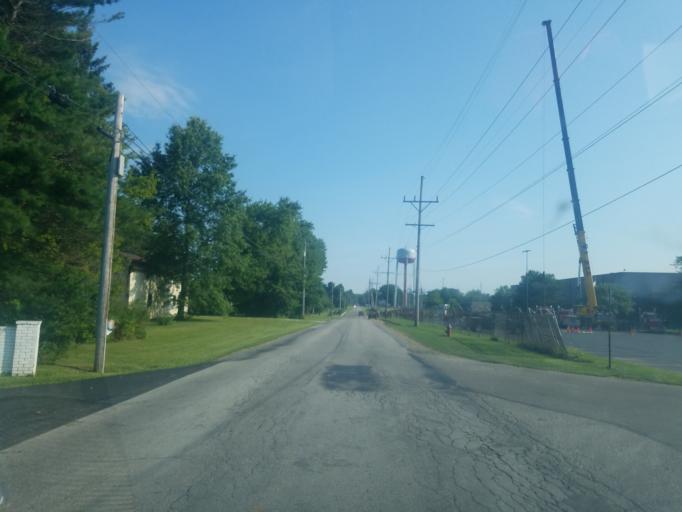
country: US
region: Ohio
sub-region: Richland County
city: Shelby
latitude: 40.8717
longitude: -82.6772
